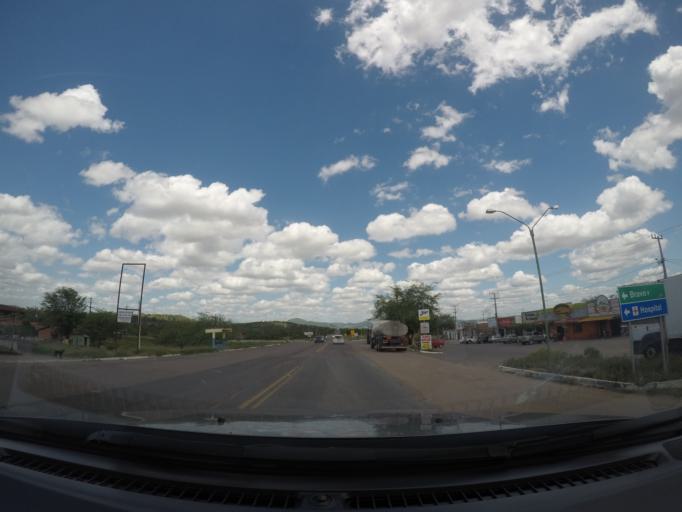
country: BR
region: Bahia
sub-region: Anguera
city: Anguera
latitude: -12.1810
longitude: -39.4544
